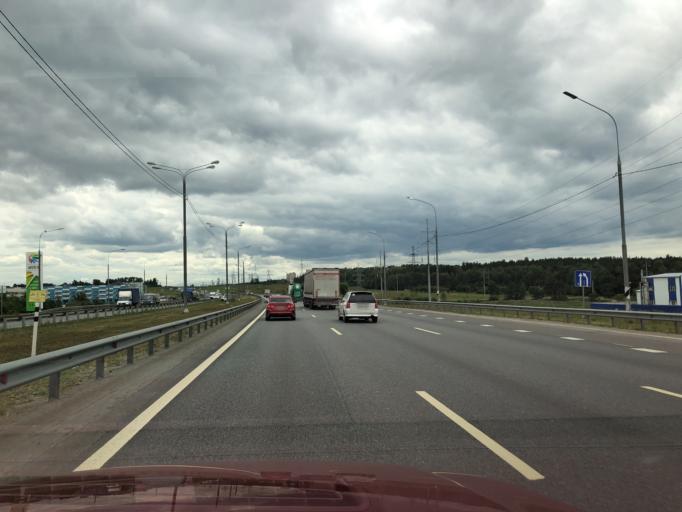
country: RU
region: Moskovskaya
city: Vostryakovo
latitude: 55.3896
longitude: 37.7758
